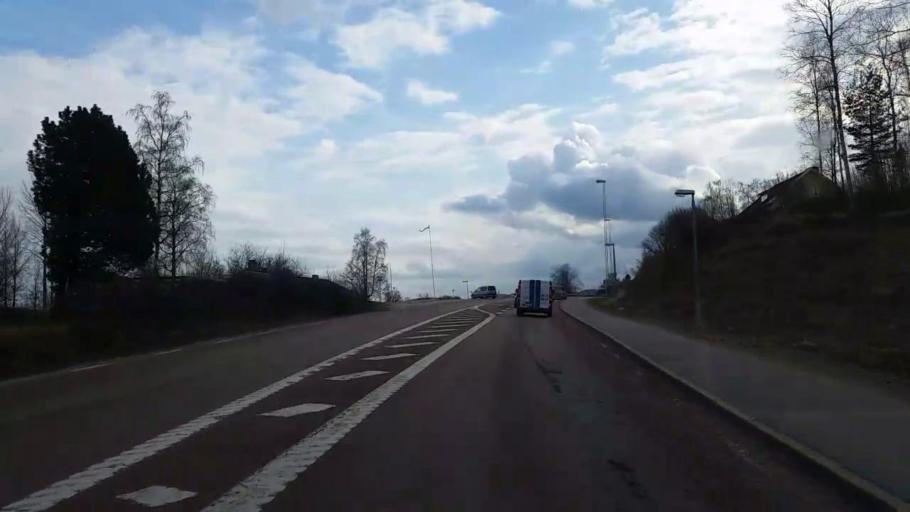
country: SE
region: Gaevleborg
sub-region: Ljusdals Kommun
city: Jaervsoe
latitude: 61.7026
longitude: 16.1653
